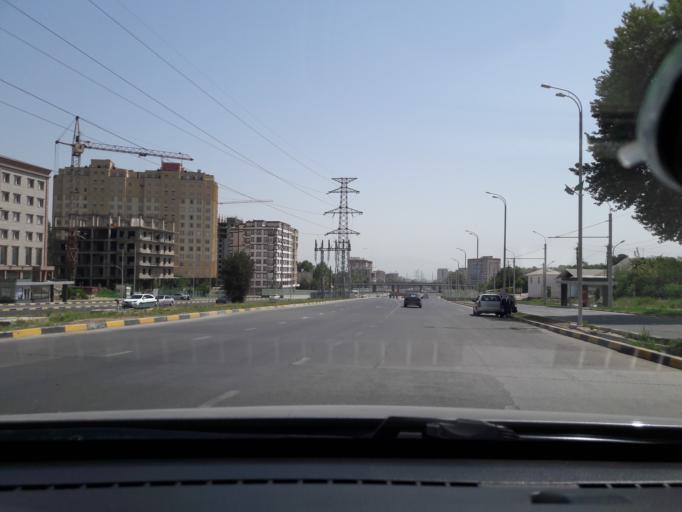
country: TJ
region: Dushanbe
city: Dushanbe
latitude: 38.5874
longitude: 68.7408
